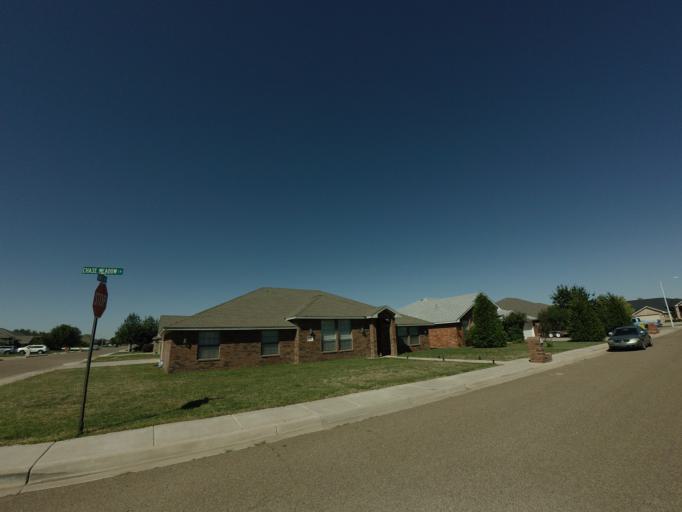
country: US
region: New Mexico
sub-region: Curry County
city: Clovis
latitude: 34.4308
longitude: -103.1701
